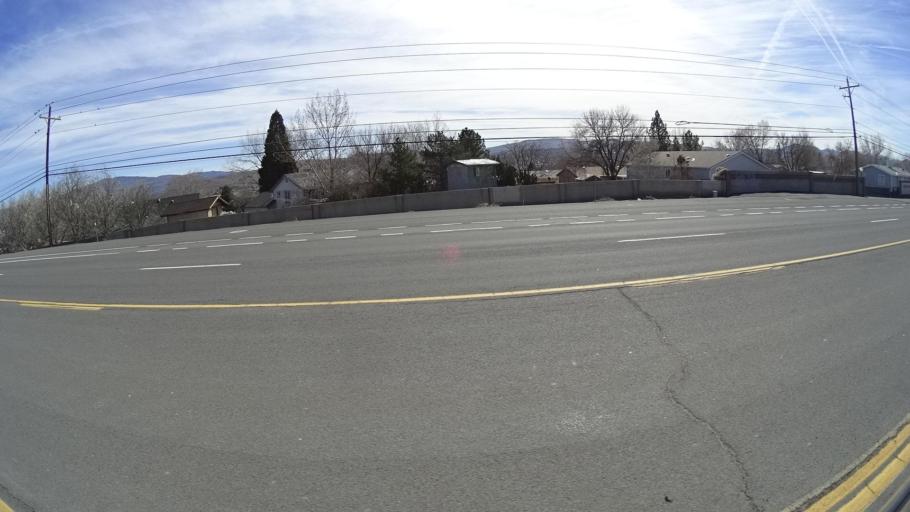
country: US
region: Nevada
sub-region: Washoe County
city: Sun Valley
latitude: 39.5912
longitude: -119.7398
